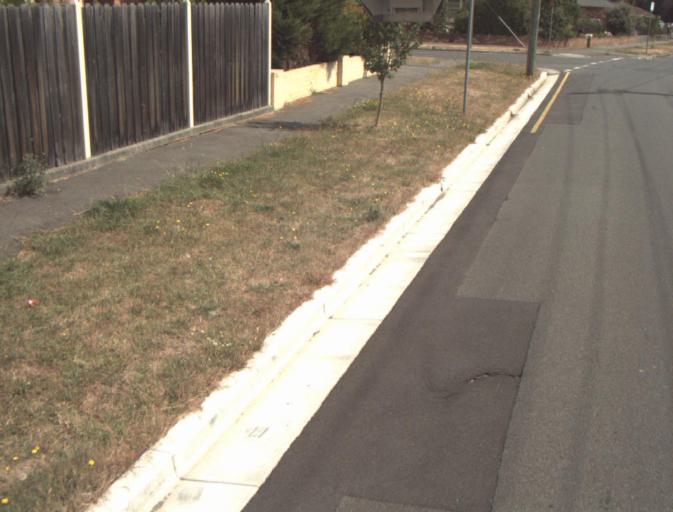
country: AU
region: Tasmania
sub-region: Launceston
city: Summerhill
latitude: -41.4696
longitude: 147.1588
